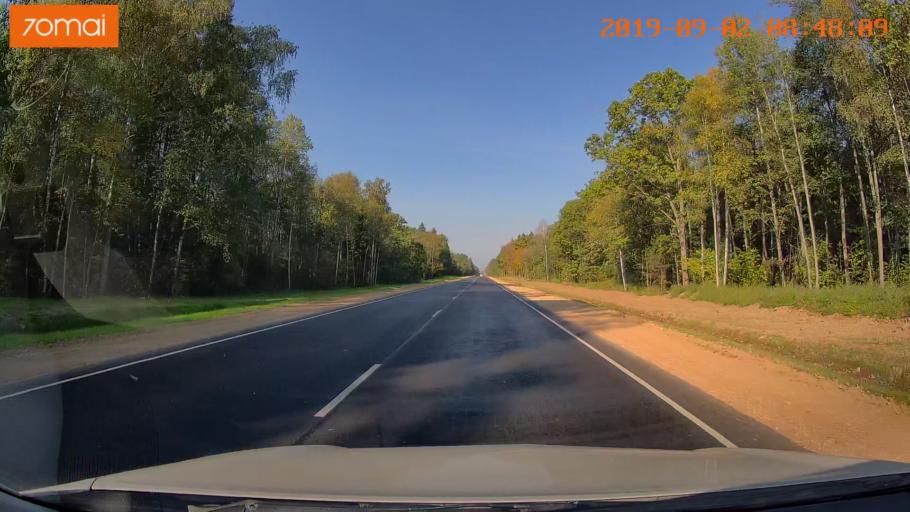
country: RU
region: Kaluga
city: Medyn'
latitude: 54.9673
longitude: 35.9395
